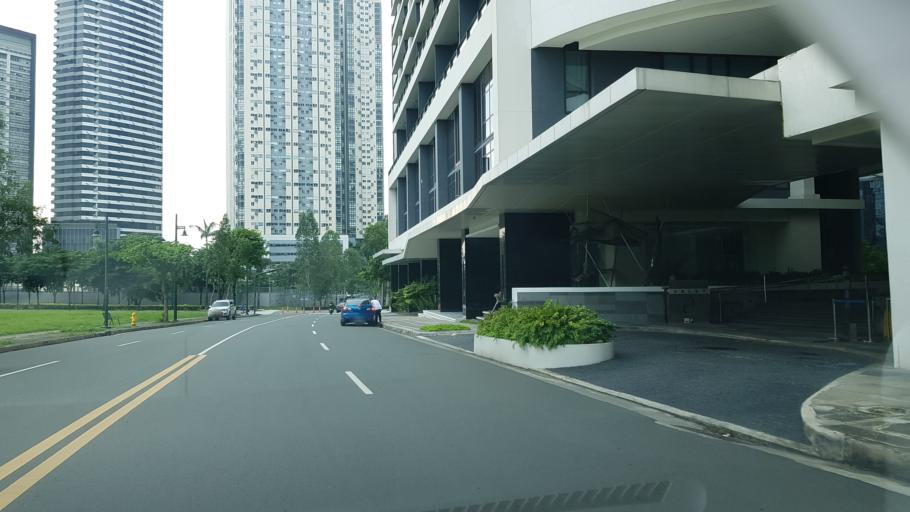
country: PH
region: Metro Manila
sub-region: Makati City
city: Makati City
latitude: 14.5457
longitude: 121.0487
